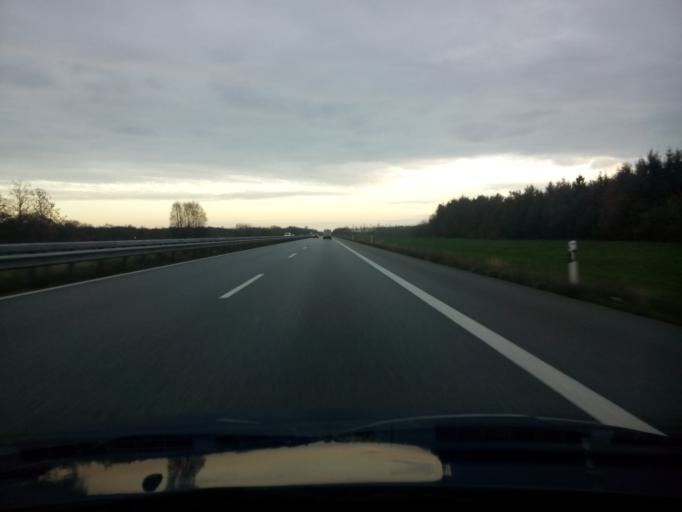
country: DE
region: Lower Saxony
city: Uthlede
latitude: 53.3477
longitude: 8.5993
